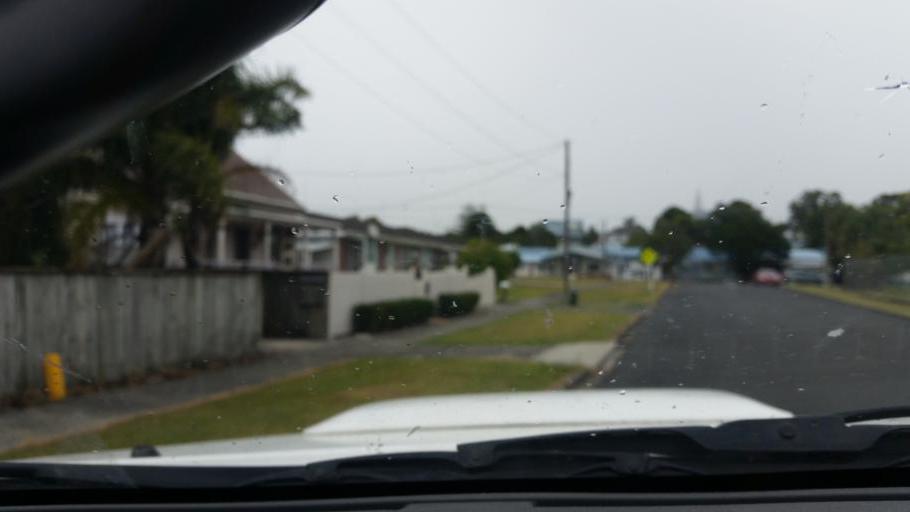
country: NZ
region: Northland
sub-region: Kaipara District
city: Dargaville
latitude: -35.9378
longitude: 173.8671
